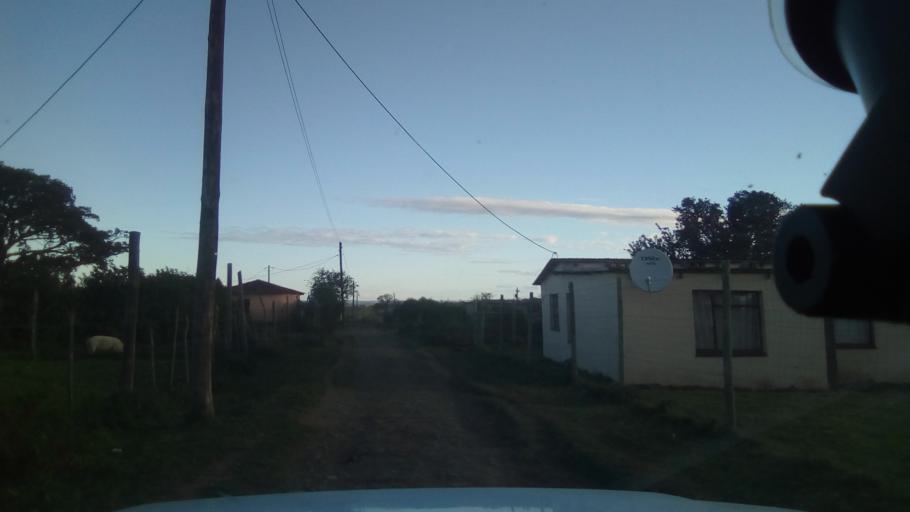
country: ZA
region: Eastern Cape
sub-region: Amathole District Municipality
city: Komga
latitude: -32.7773
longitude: 27.9387
